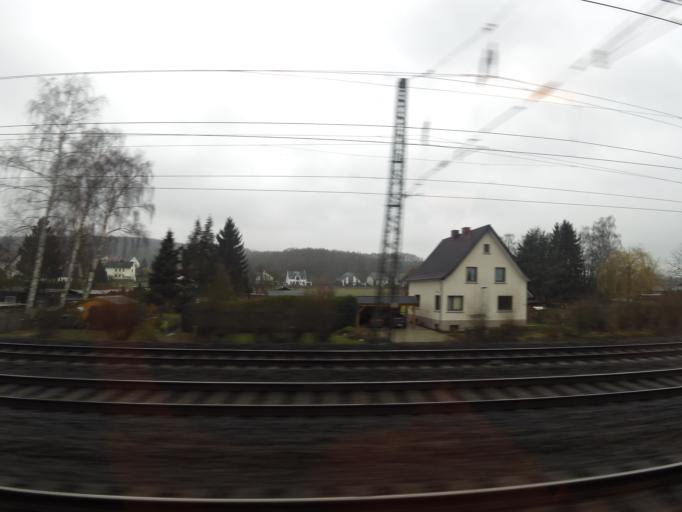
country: DE
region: North Rhine-Westphalia
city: Loehne
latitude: 52.1575
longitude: 8.6679
